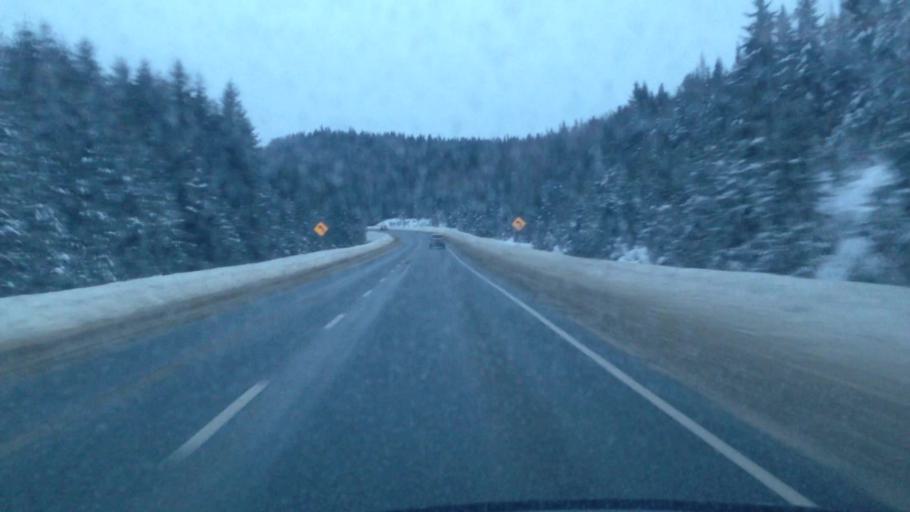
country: CA
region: Quebec
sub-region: Laurentides
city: Sainte-Agathe-des-Monts
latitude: 46.1145
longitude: -74.4282
